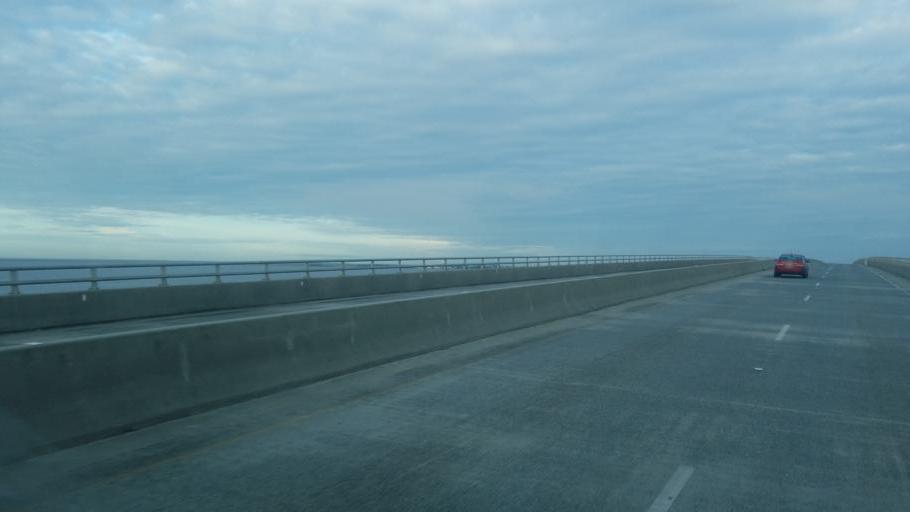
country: US
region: North Carolina
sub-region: Dare County
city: Manteo
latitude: 35.8851
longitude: -75.7142
